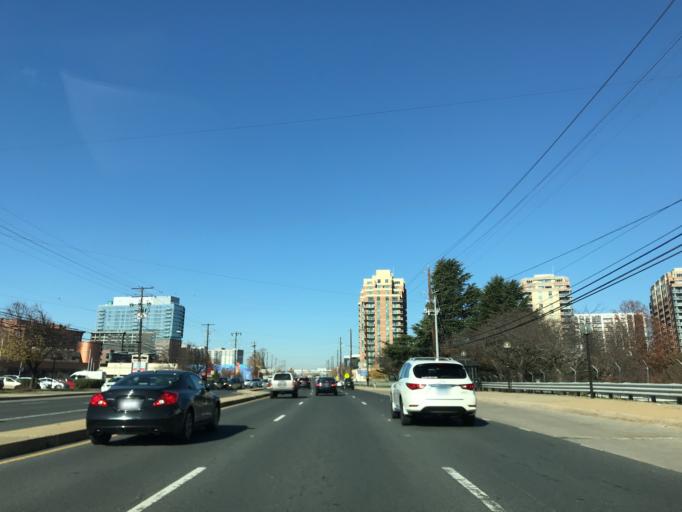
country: US
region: Maryland
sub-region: Montgomery County
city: North Bethesda
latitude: 39.0474
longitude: -77.1129
